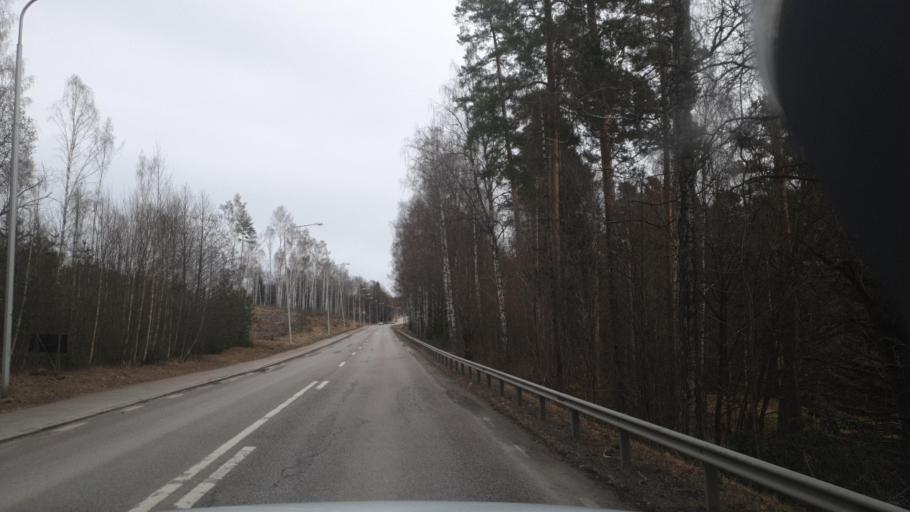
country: SE
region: Vaermland
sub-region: Arvika Kommun
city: Arvika
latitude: 59.6695
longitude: 12.4811
